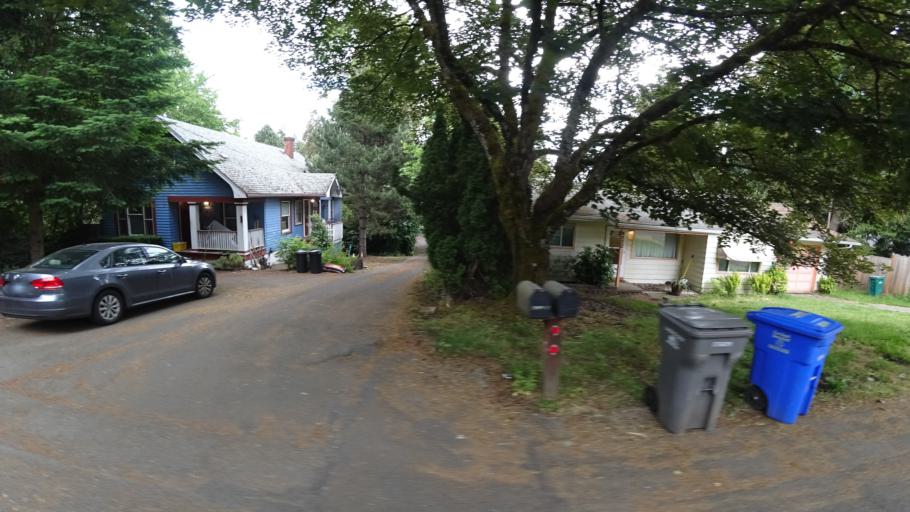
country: US
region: Oregon
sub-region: Clackamas County
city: Lake Oswego
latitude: 45.4585
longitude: -122.7057
